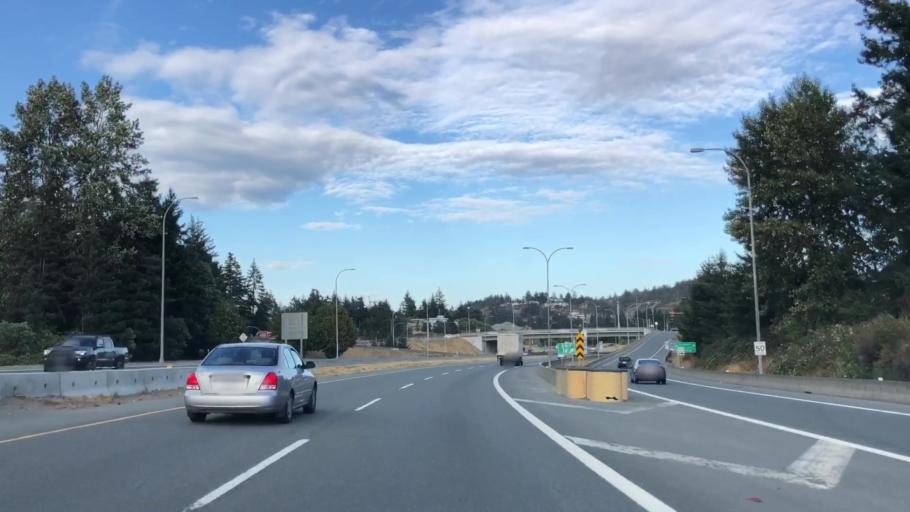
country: CA
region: British Columbia
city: Langford
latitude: 48.4560
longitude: -123.5012
